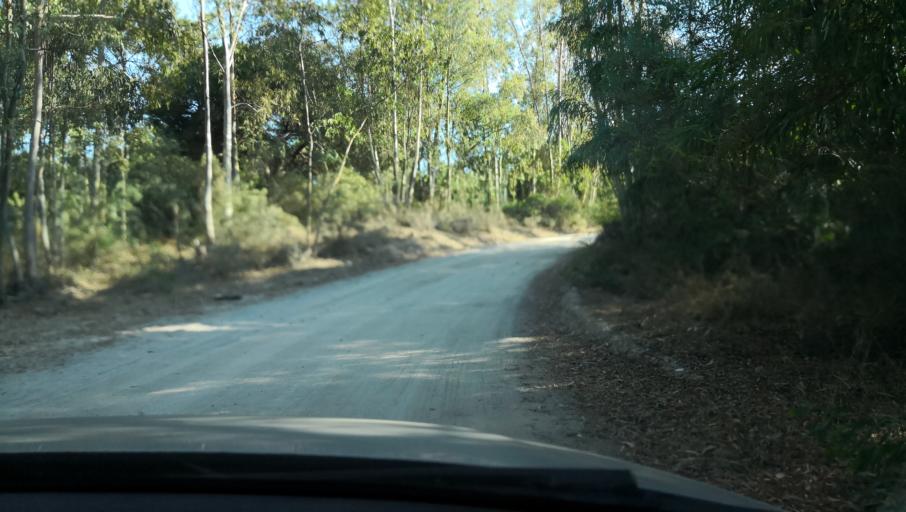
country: PT
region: Setubal
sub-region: Setubal
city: Setubal
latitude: 38.4747
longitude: -8.8789
